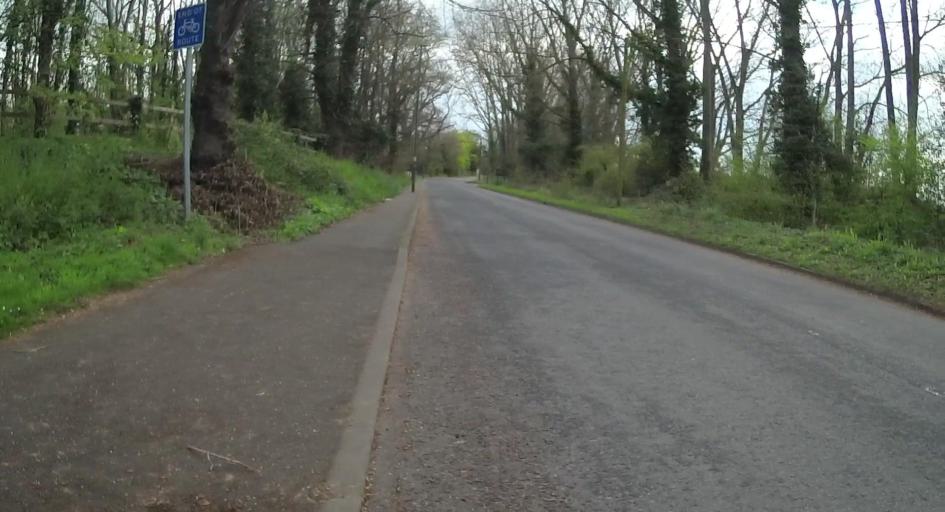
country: GB
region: England
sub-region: Surrey
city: Shepperton
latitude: 51.3899
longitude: -0.4633
